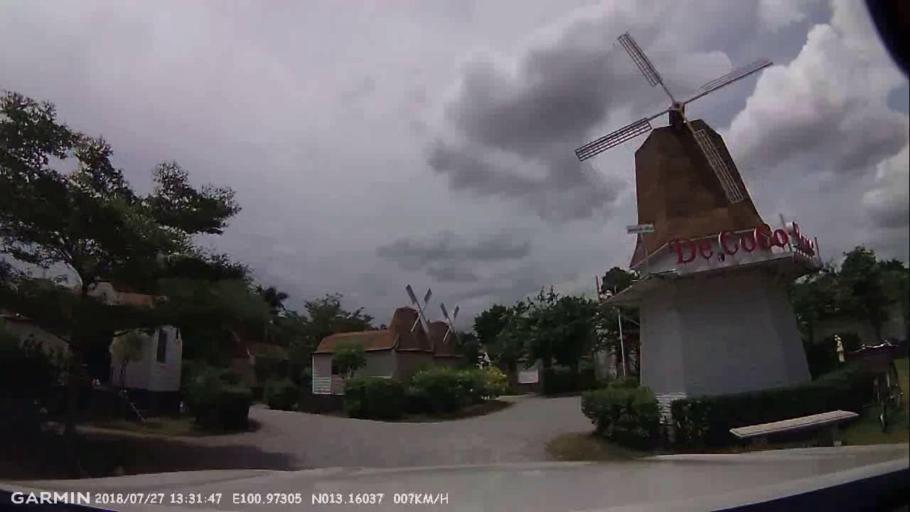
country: TH
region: Chon Buri
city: Si Racha
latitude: 13.1604
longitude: 100.9730
